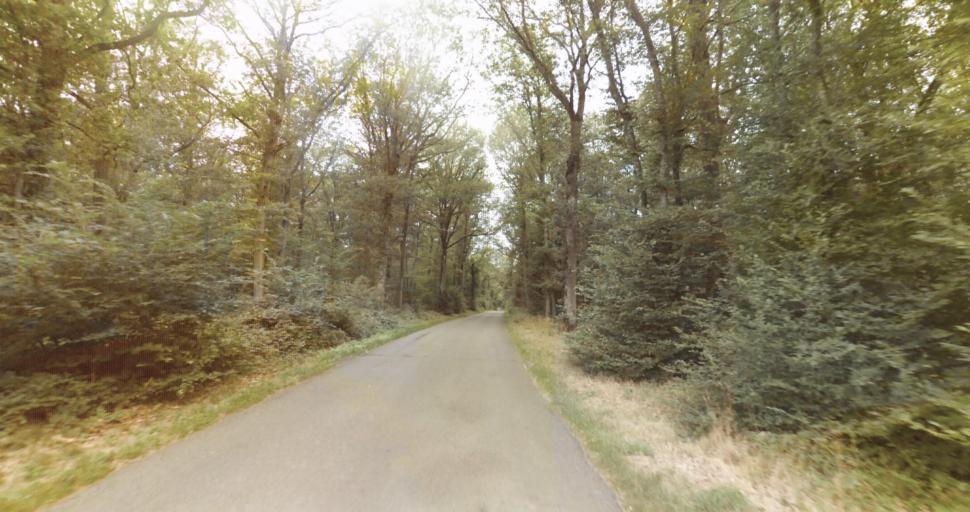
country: FR
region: Haute-Normandie
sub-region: Departement de l'Eure
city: Marcilly-sur-Eure
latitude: 48.8680
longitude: 1.3395
